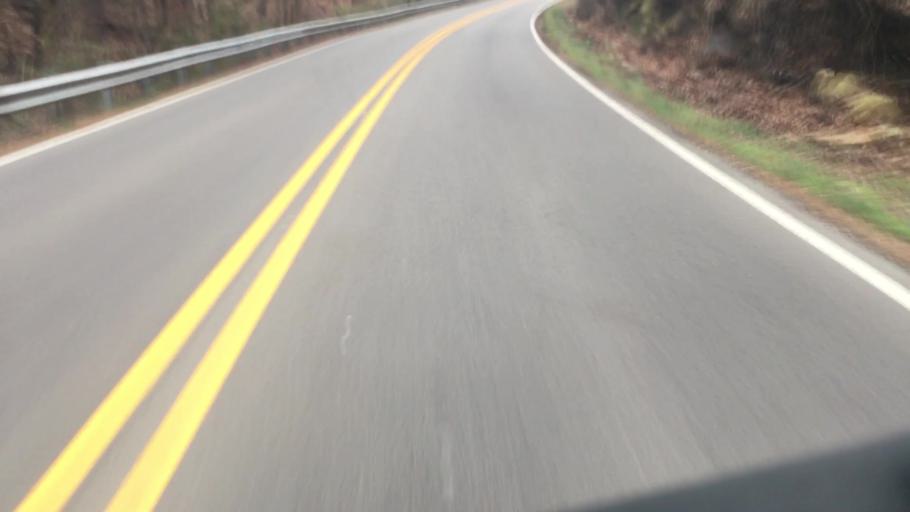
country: US
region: Alabama
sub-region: Jefferson County
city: Vestavia Hills
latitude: 33.4575
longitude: -86.7617
